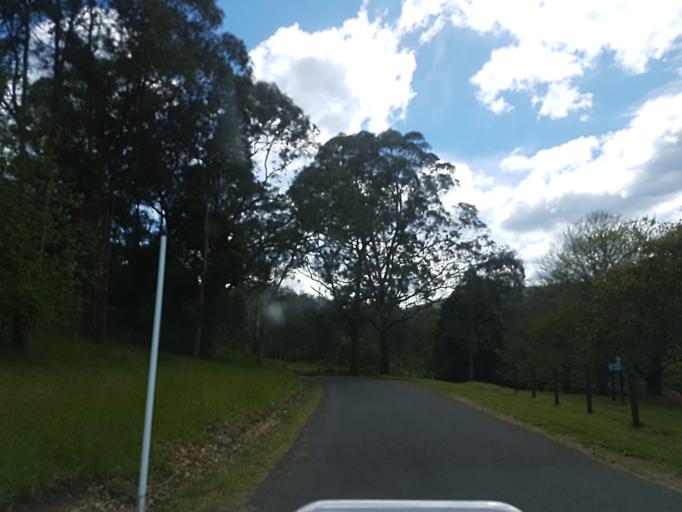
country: AU
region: Victoria
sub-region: East Gippsland
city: Bairnsdale
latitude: -37.4312
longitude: 147.2514
